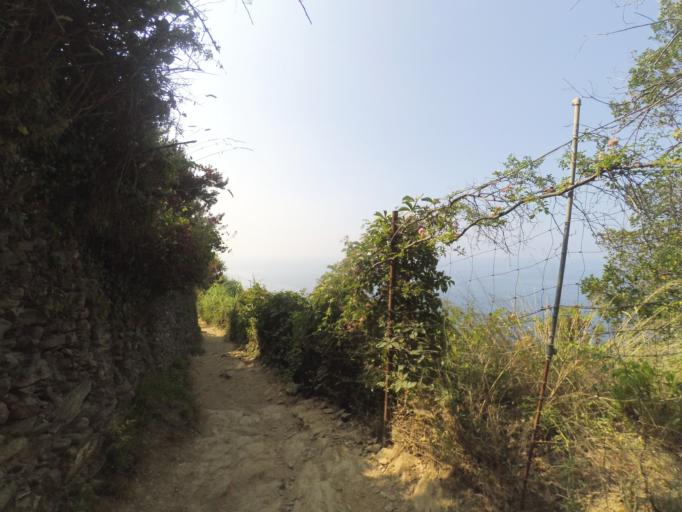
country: IT
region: Liguria
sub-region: Provincia di La Spezia
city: Vernazza
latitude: 44.1379
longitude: 9.6800
